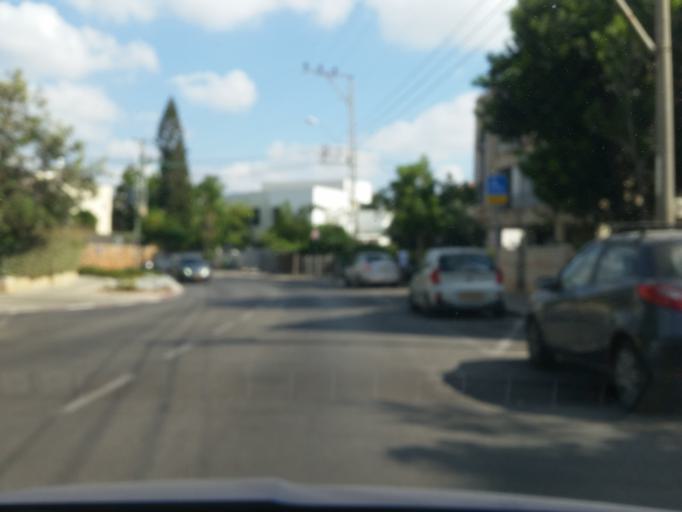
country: IL
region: Tel Aviv
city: Ramat HaSharon
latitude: 32.1157
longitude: 34.8314
